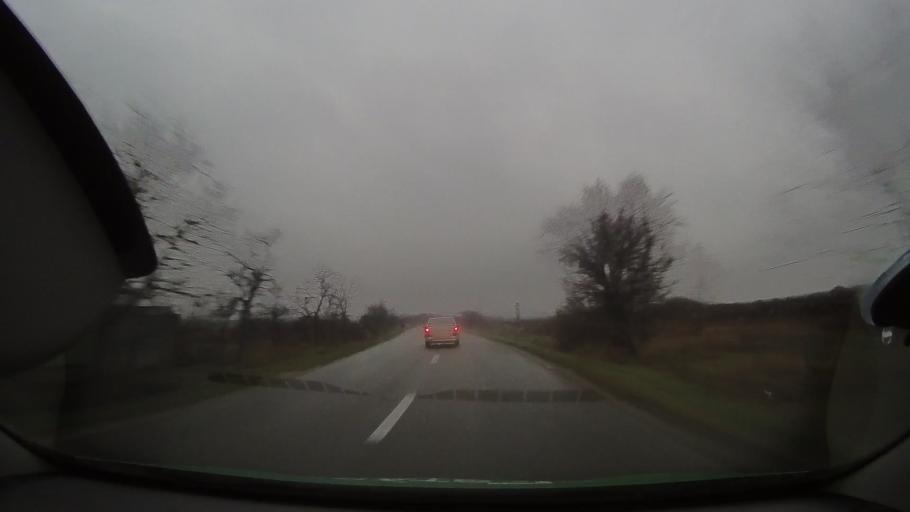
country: RO
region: Arad
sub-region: Comuna Craiova
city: Craiova
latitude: 46.5487
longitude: 21.9601
